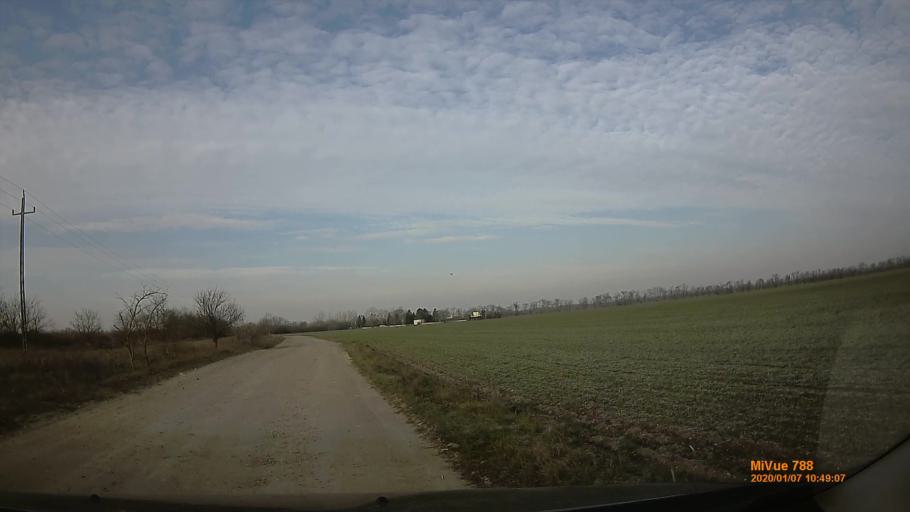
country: HU
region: Gyor-Moson-Sopron
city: Rajka
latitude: 47.9150
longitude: 17.1762
